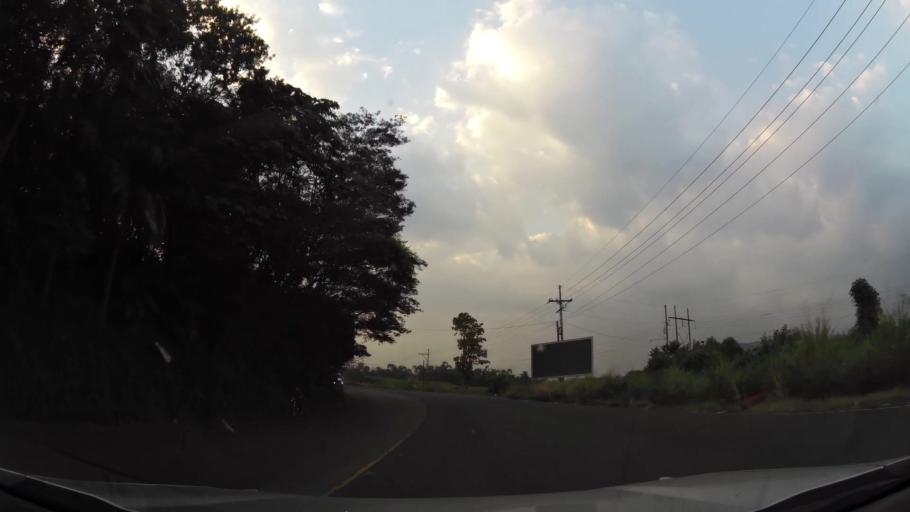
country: GT
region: Escuintla
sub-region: Municipio de La Democracia
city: La Democracia
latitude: 14.2710
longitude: -90.8994
